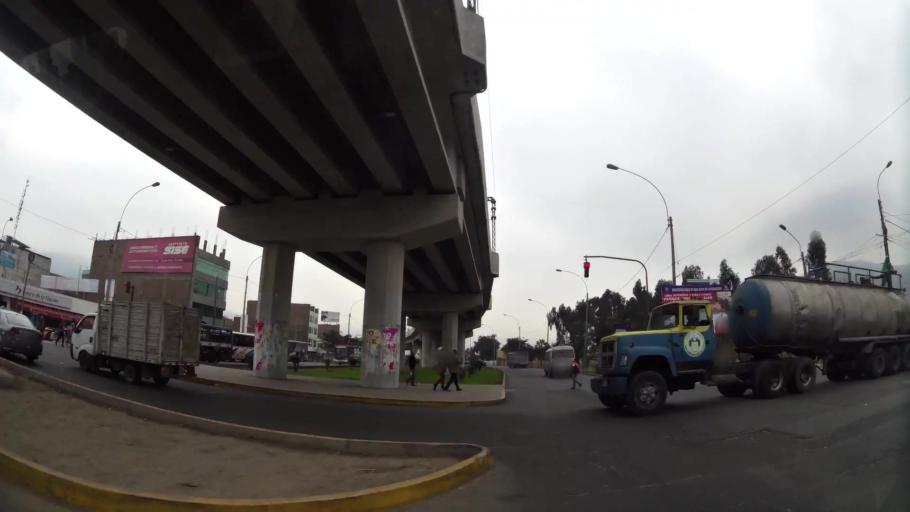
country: PE
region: Lima
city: Lima
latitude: -12.0132
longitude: -77.0019
